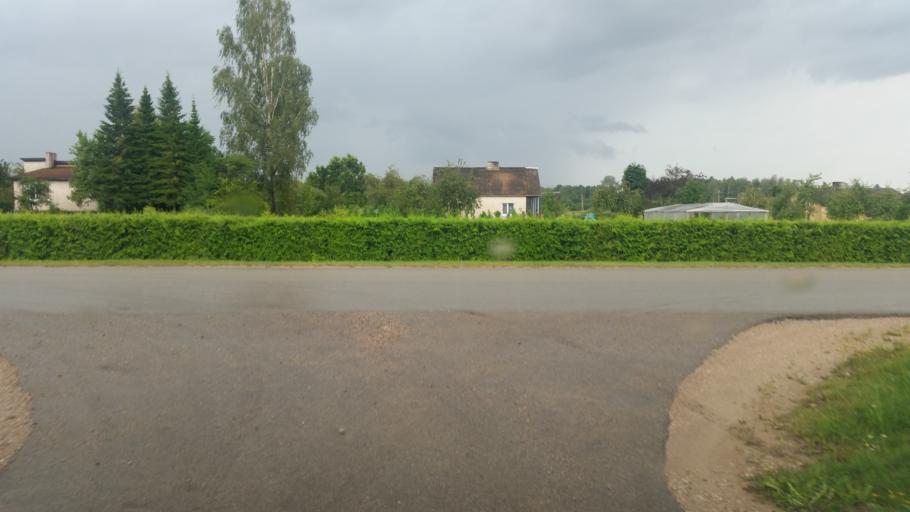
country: LV
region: Vecumnieki
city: Vecumnieki
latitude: 56.4325
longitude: 24.4618
